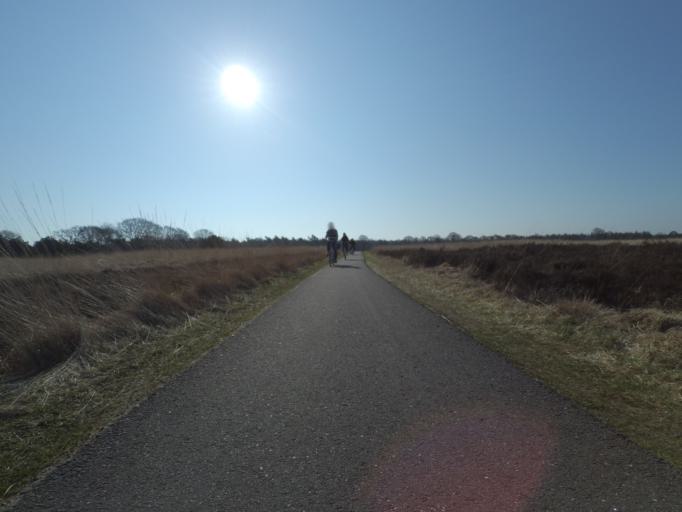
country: NL
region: Gelderland
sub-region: Gemeente Renkum
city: Wolfheze
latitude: 52.0443
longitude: 5.8313
